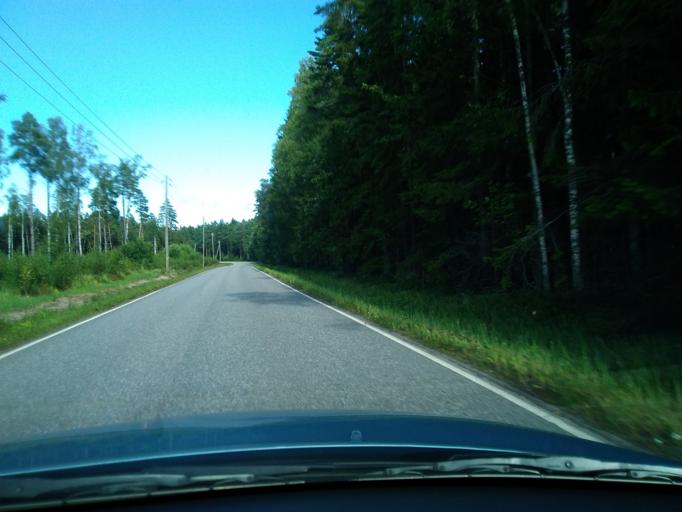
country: FI
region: Uusimaa
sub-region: Raaseporin
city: Hanko
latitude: 59.8370
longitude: 23.1558
